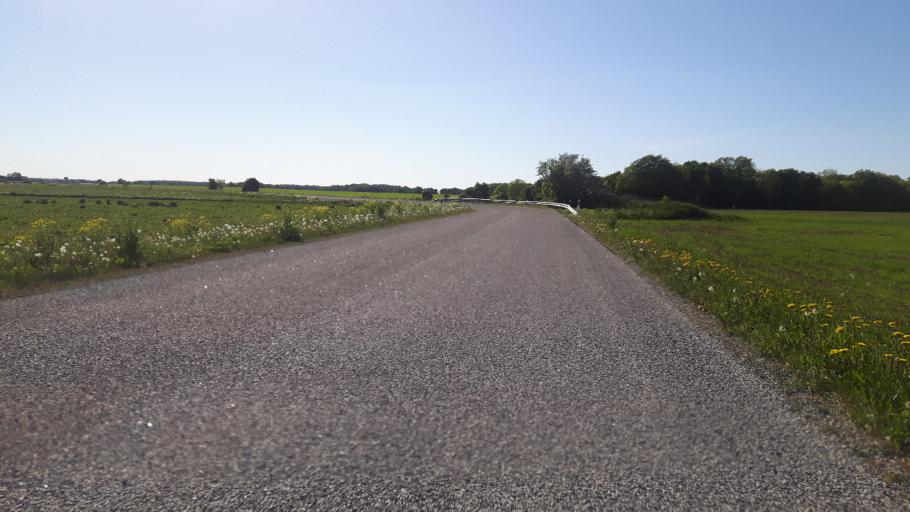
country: EE
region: Ida-Virumaa
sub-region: Kohtla-Jaerve linn
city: Kohtla-Jarve
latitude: 59.4401
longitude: 27.2743
